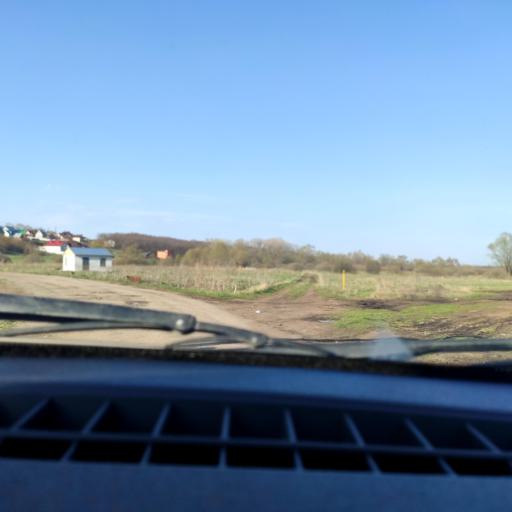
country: RU
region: Bashkortostan
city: Mikhaylovka
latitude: 54.8225
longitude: 55.9105
